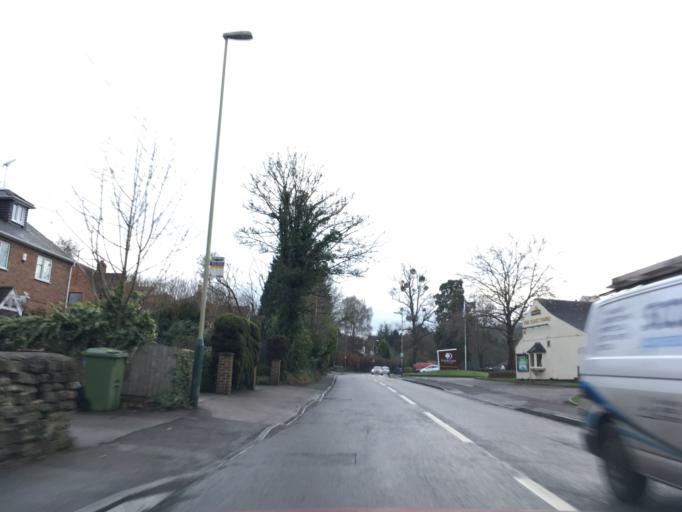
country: GB
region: England
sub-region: Gloucestershire
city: Charlton Kings
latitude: 51.8754
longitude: -2.0526
